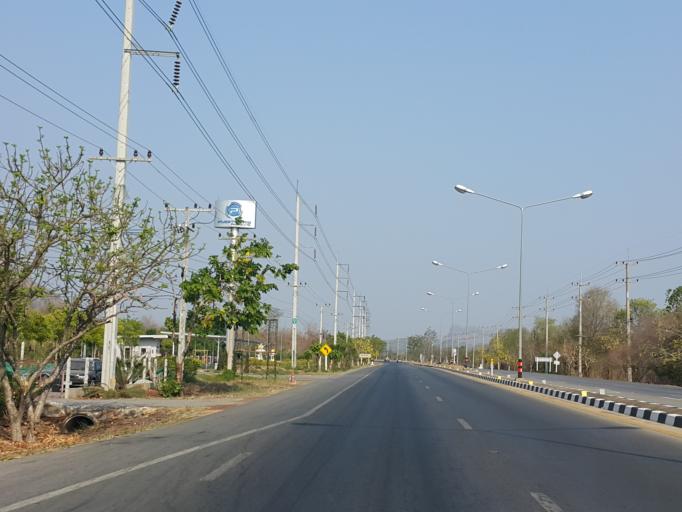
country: TH
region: Kanchanaburi
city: Kanchanaburi
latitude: 14.0675
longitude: 99.4099
